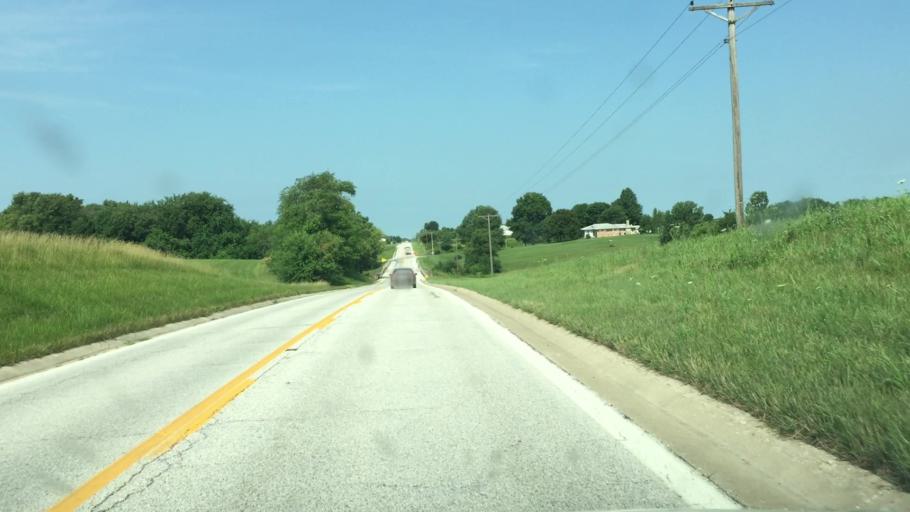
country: US
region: Illinois
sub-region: Hancock County
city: Nauvoo
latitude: 40.5517
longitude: -91.3227
